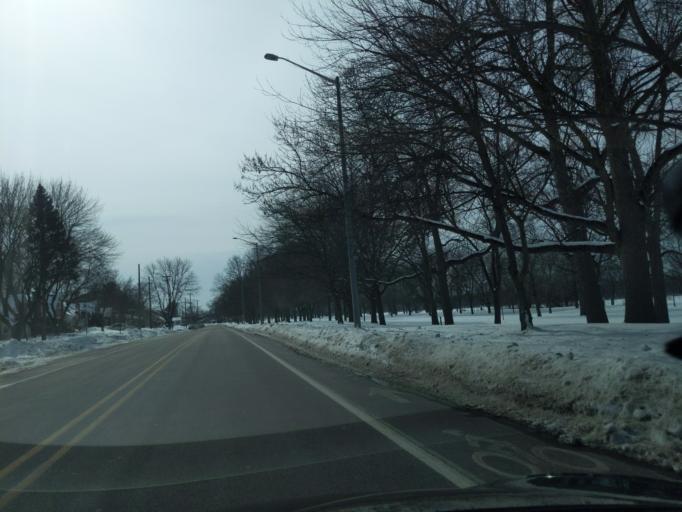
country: US
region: Michigan
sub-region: Kent County
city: Comstock Park
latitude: 43.0030
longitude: -85.6694
